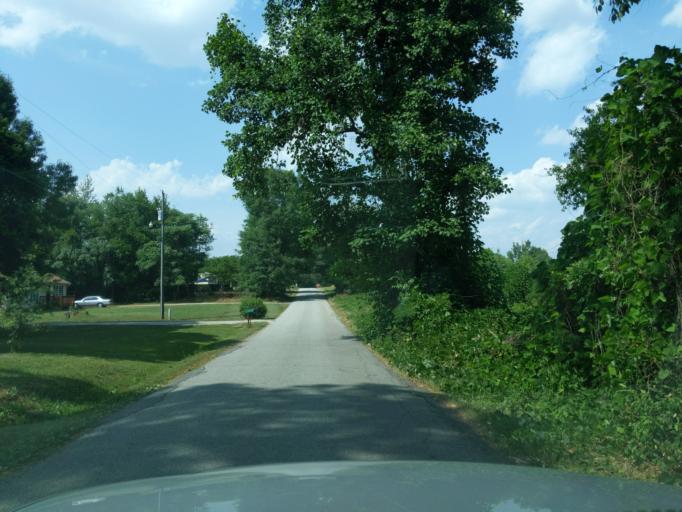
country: US
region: South Carolina
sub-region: Spartanburg County
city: Wellford
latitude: 34.9121
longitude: -82.0596
